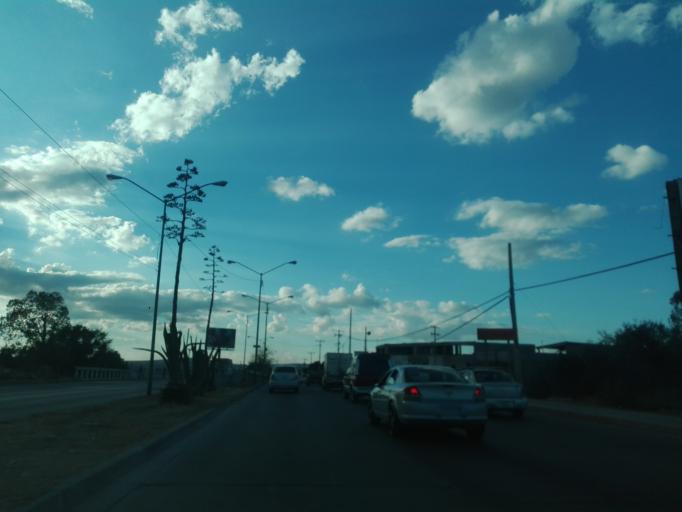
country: MX
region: Guanajuato
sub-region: Leon
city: San Jose de Duran (Los Troncoso)
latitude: 21.0888
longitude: -101.6740
